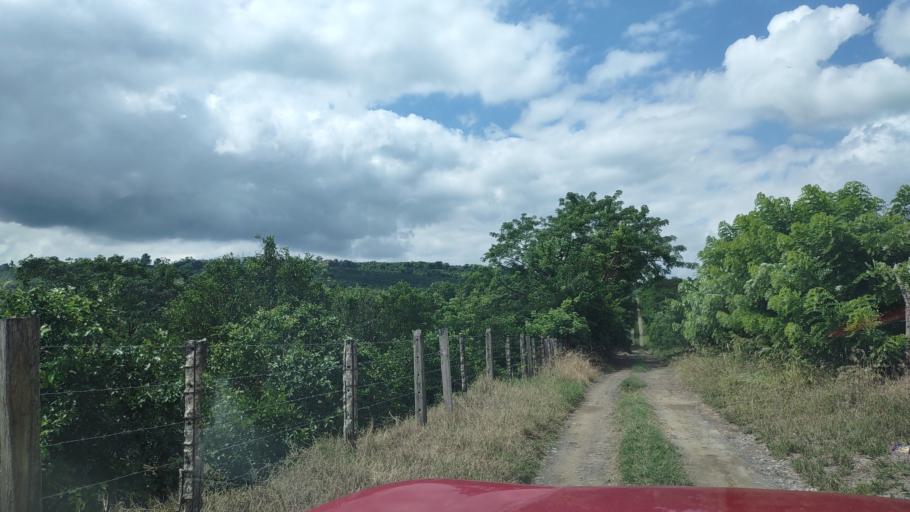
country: MX
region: Puebla
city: San Jose Acateno
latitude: 20.2223
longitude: -97.1506
